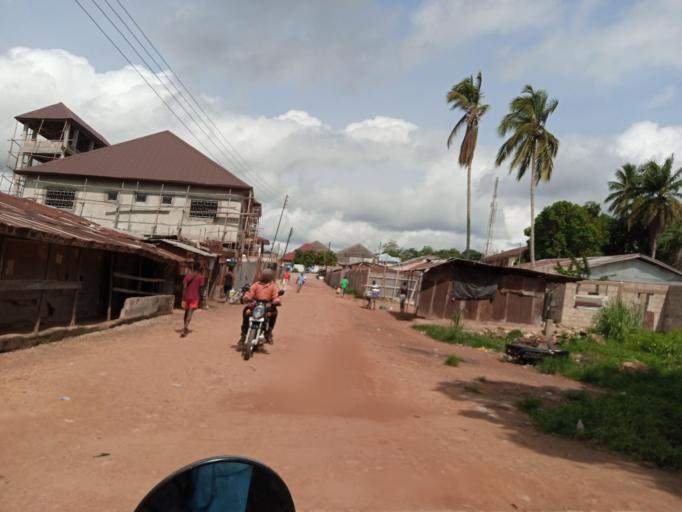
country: SL
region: Southern Province
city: Bo
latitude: 7.9614
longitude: -11.7386
